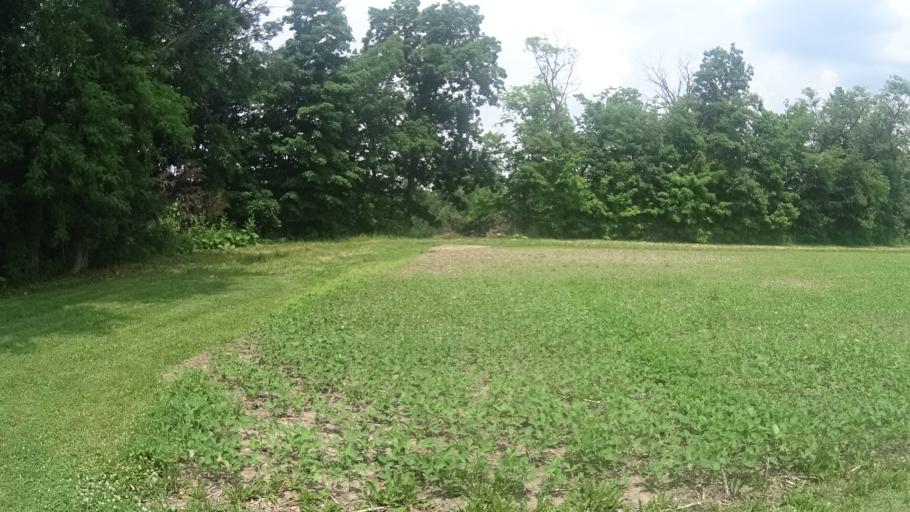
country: US
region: Ohio
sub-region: Huron County
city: Monroeville
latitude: 41.2867
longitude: -82.6665
